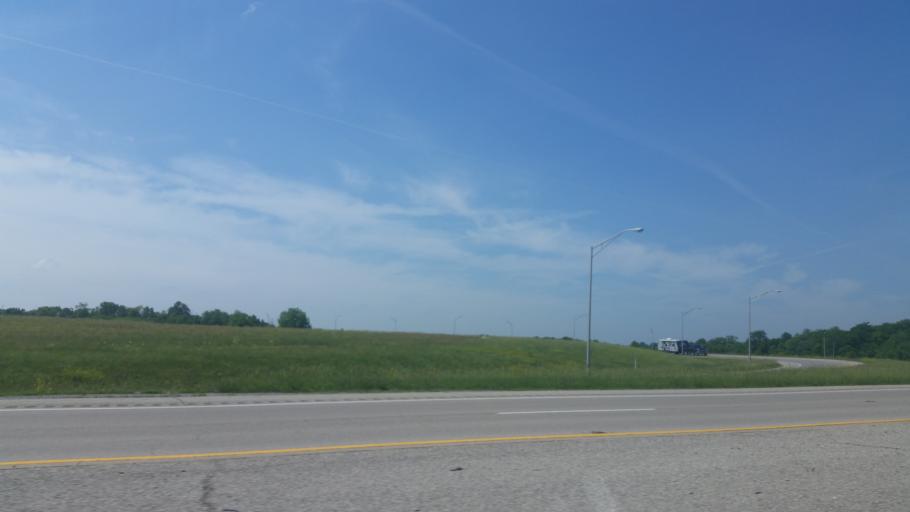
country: US
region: Kentucky
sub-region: Campbell County
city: Cold Spring
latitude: 39.0021
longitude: -84.4233
